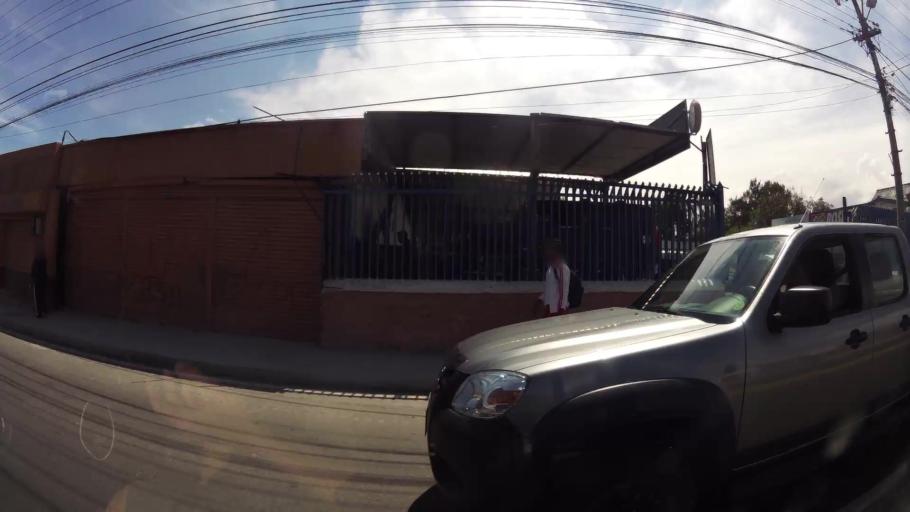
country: EC
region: Pichincha
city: Quito
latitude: -0.2141
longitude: -78.4077
